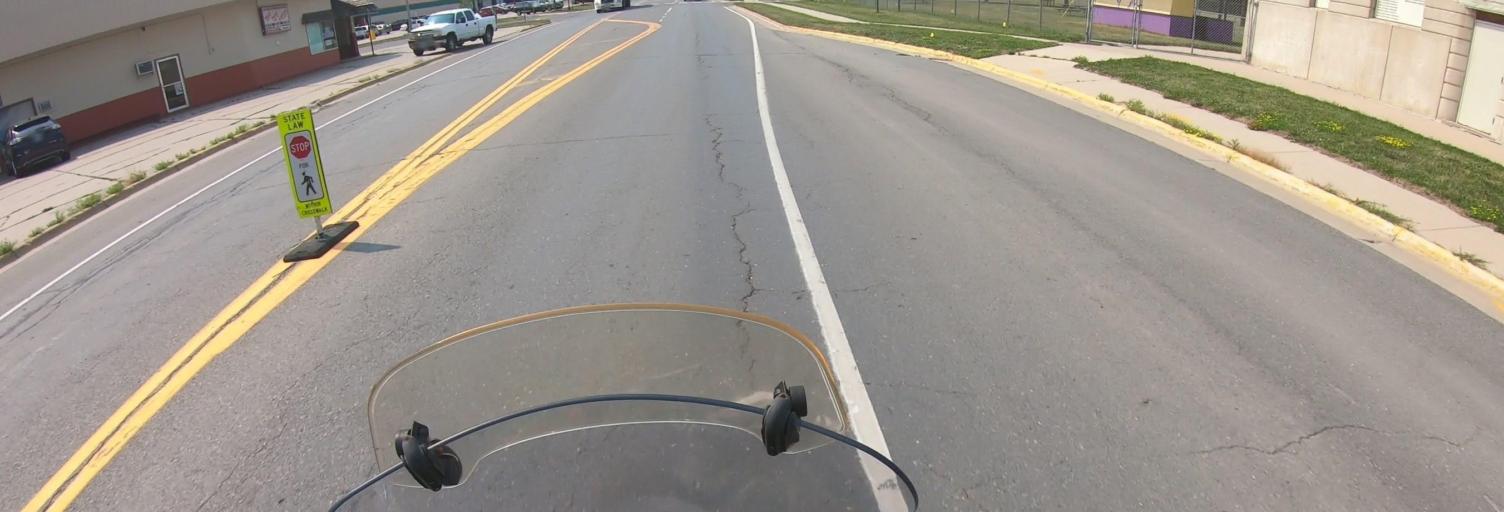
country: US
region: Minnesota
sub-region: Koochiching County
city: International Falls
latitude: 48.6003
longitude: -93.4186
